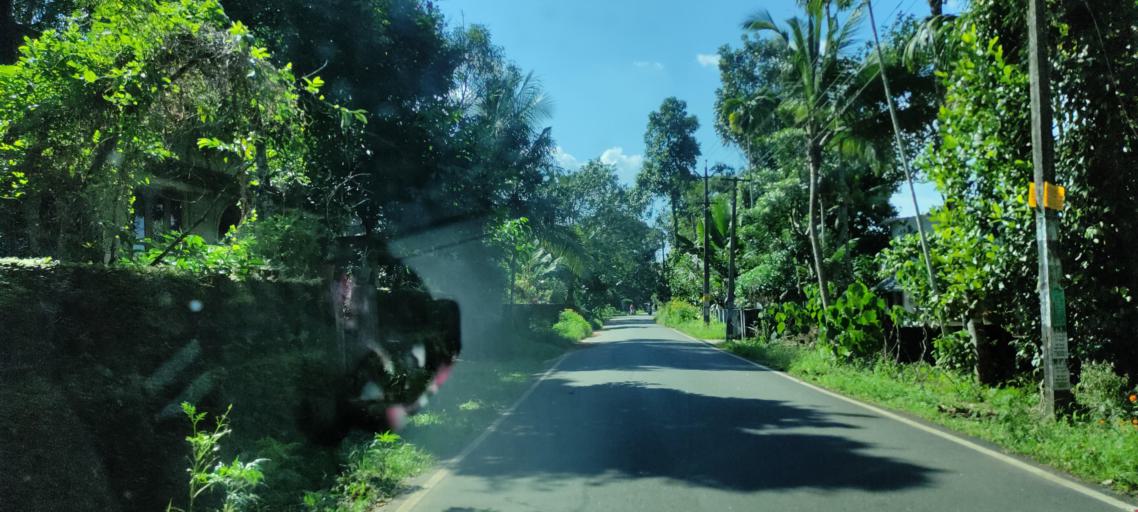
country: IN
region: Kerala
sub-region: Pattanamtitta
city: Adur
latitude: 9.1997
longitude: 76.7551
